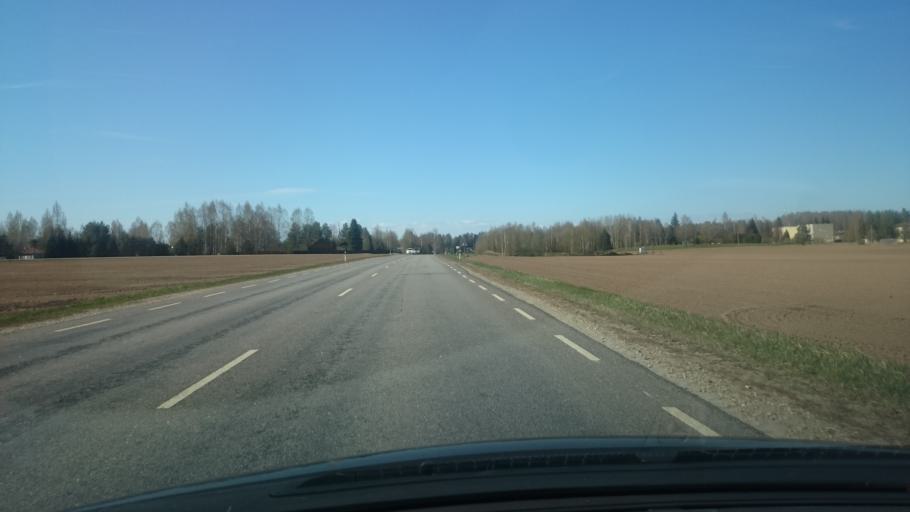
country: EE
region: Tartu
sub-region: UElenurme vald
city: Ulenurme
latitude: 58.3264
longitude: 26.9810
